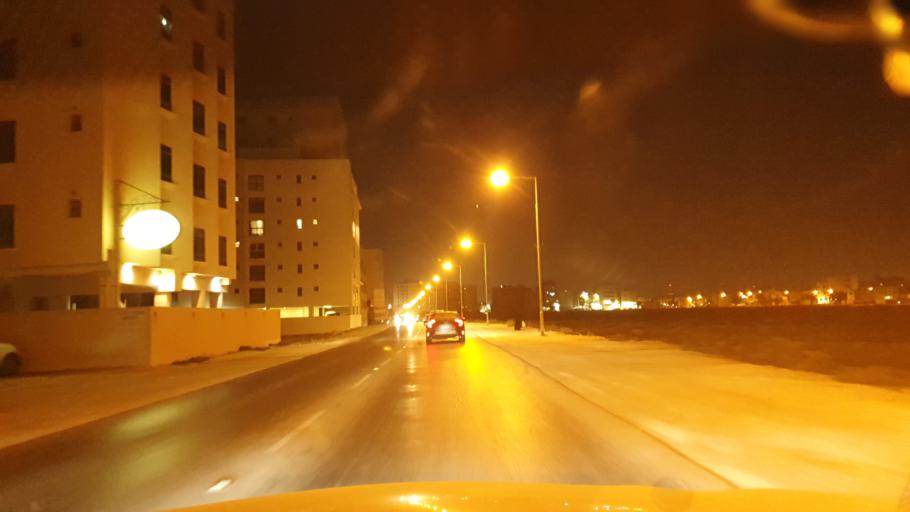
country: BH
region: Northern
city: Madinat `Isa
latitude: 26.1847
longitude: 50.4820
